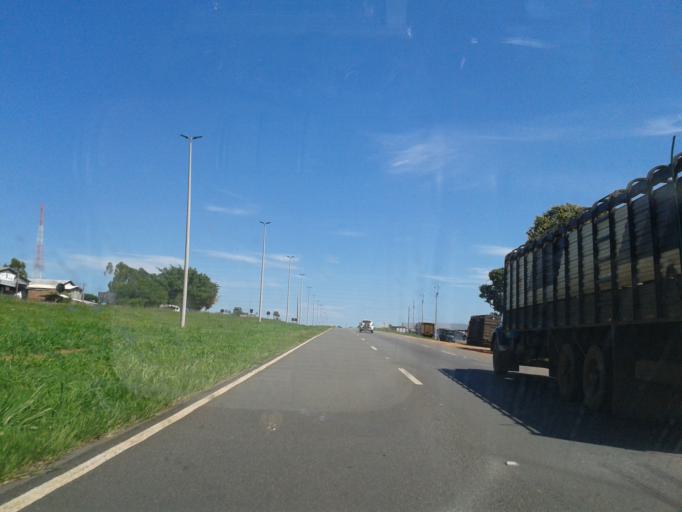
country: BR
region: Goias
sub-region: Bela Vista De Goias
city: Bela Vista de Goias
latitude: -16.9510
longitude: -48.9629
